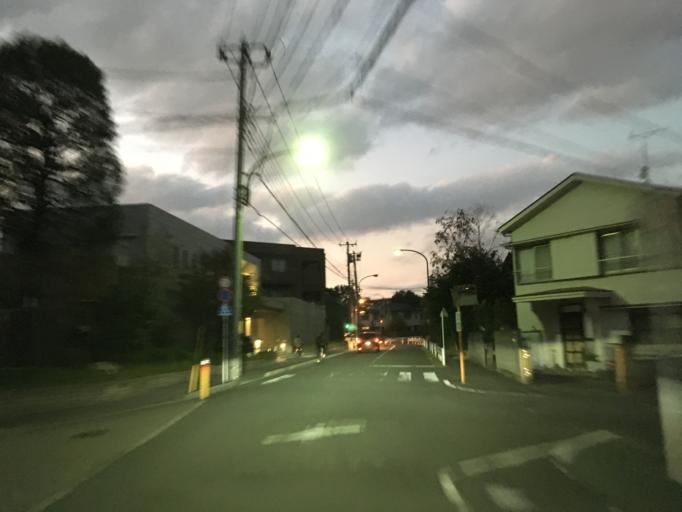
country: JP
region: Tokyo
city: Kokubunji
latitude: 35.7177
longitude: 139.4397
